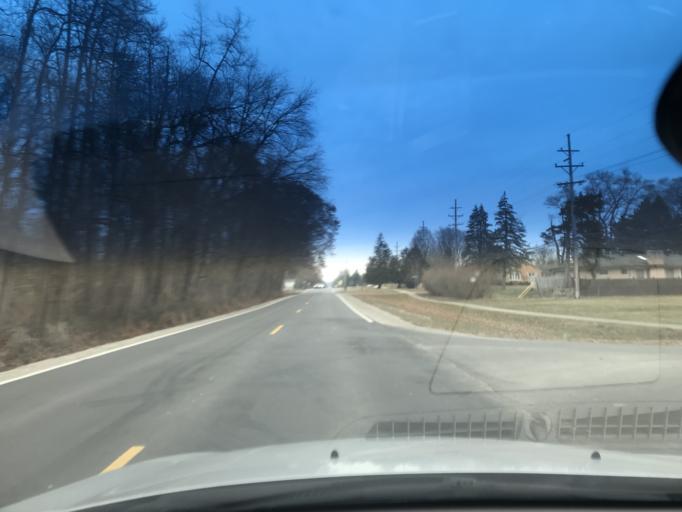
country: US
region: Michigan
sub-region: Macomb County
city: Shelby
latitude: 42.6855
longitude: -83.0541
